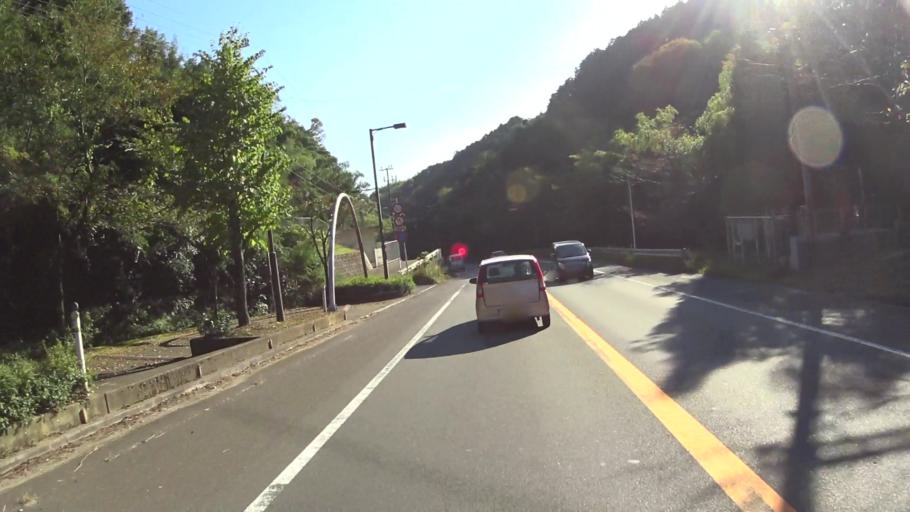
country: JP
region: Kyoto
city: Miyazu
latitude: 35.5437
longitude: 135.1110
